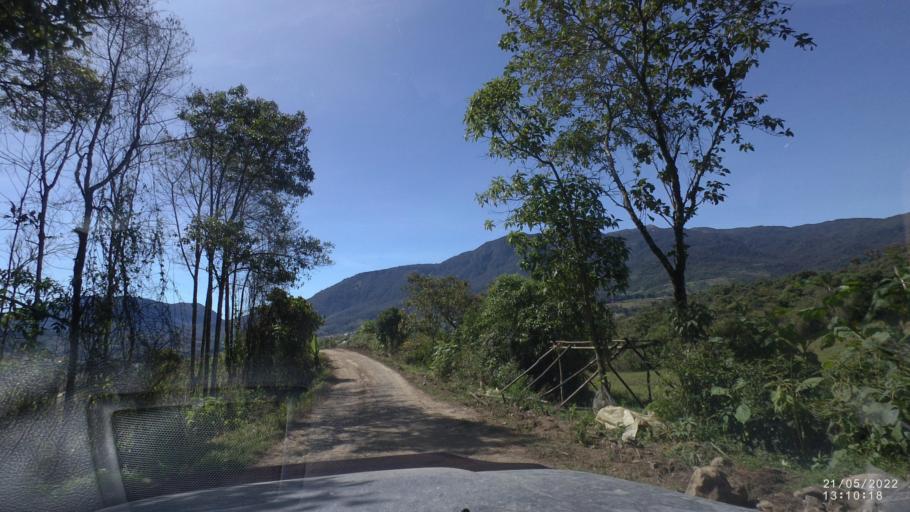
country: BO
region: Cochabamba
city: Colomi
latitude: -17.1416
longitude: -65.9424
